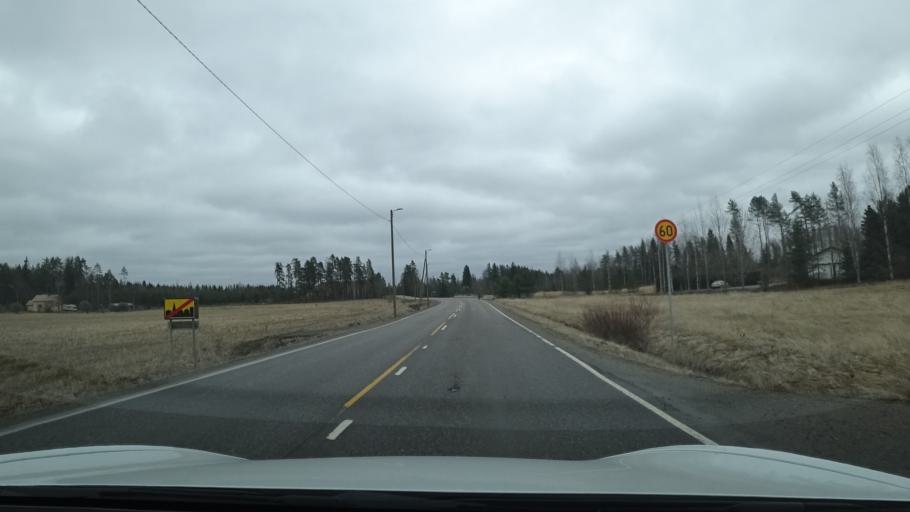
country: FI
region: Uusimaa
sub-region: Helsinki
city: Pornainen
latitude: 60.4843
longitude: 25.3737
